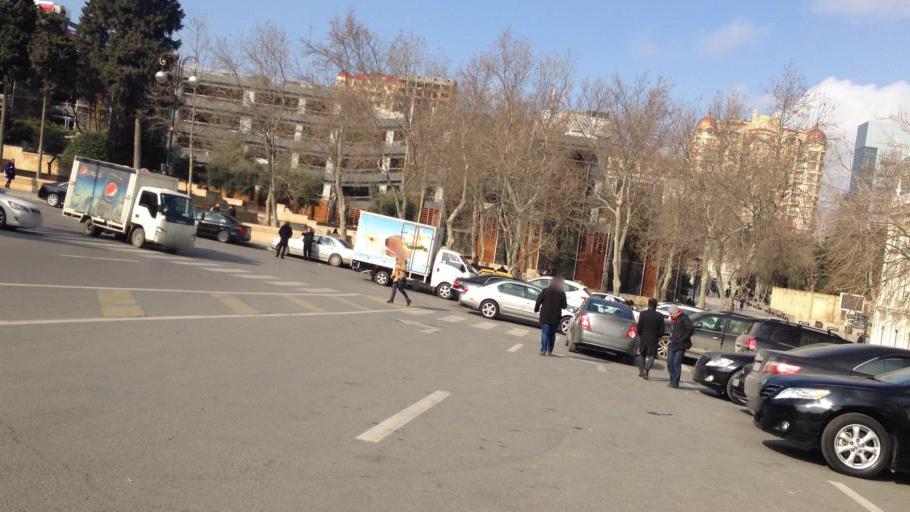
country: AZ
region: Baki
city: Badamdar
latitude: 40.3692
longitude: 49.8362
